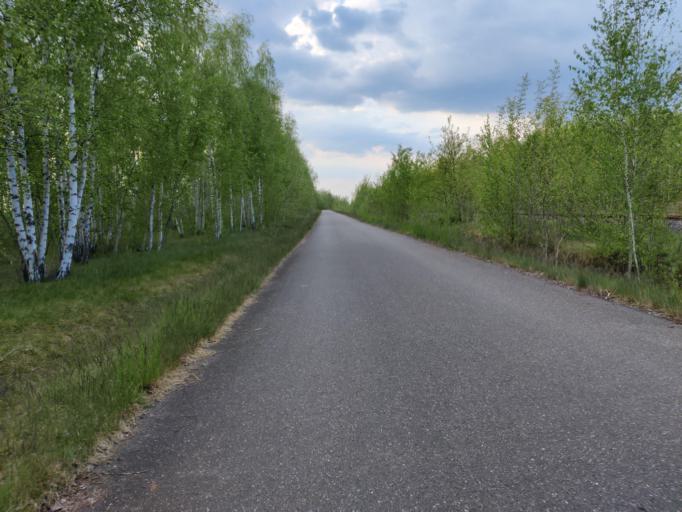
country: DE
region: Saxony
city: Rotha
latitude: 51.2155
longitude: 12.4308
